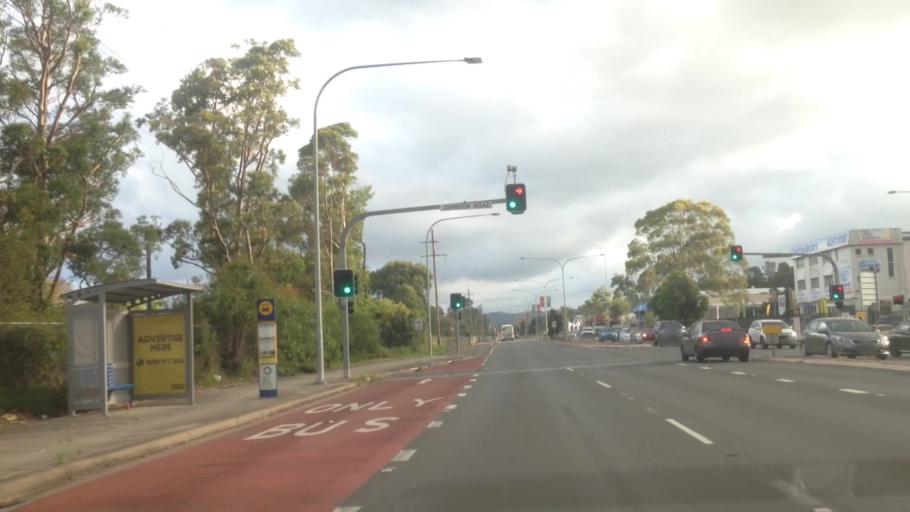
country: AU
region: New South Wales
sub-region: Wyong Shire
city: Chittaway Bay
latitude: -33.2943
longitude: 151.4228
